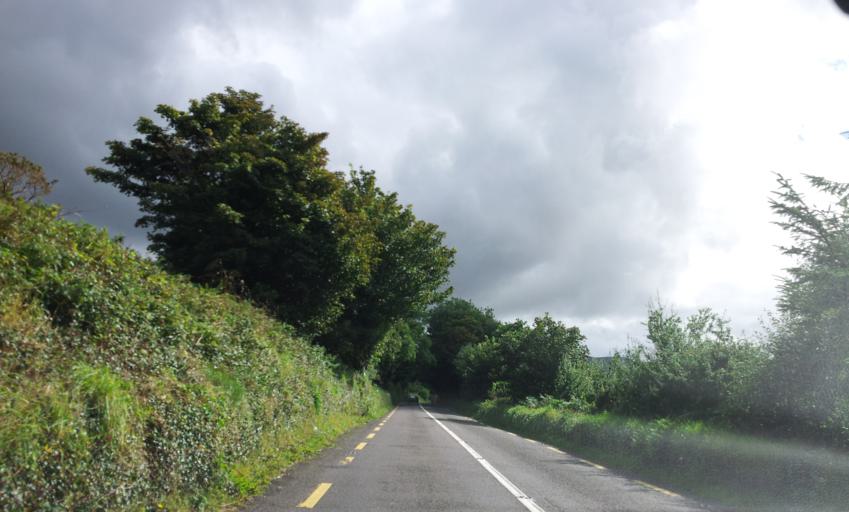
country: IE
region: Munster
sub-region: Ciarrai
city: Killorglin
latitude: 52.2232
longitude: -9.9019
